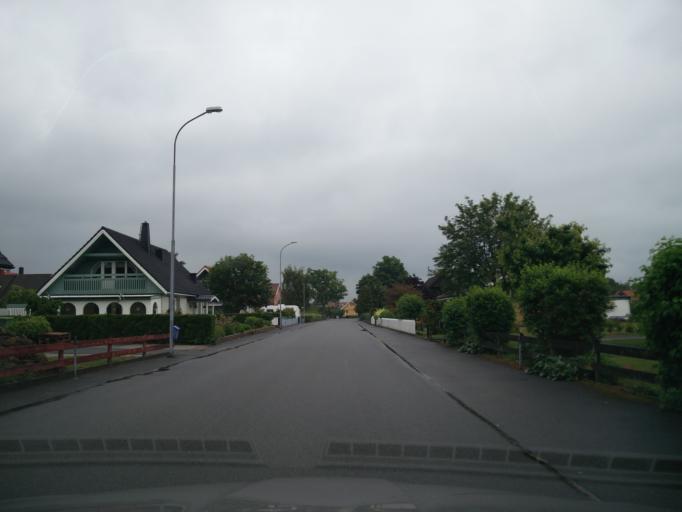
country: SE
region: Skane
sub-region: Hassleholms Kommun
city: Vinslov
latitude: 56.1014
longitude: 13.9012
